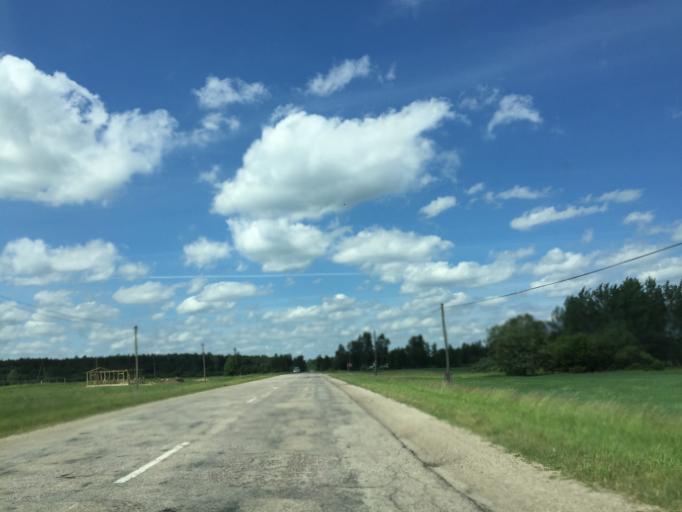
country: LV
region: Engure
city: Smarde
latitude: 56.9604
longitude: 23.3345
